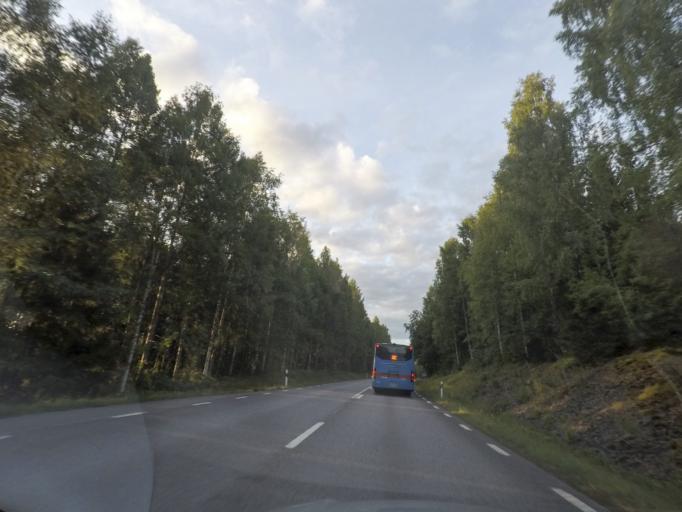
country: SE
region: OErebro
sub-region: Hallefors Kommun
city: Haellefors
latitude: 59.6978
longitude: 14.5474
